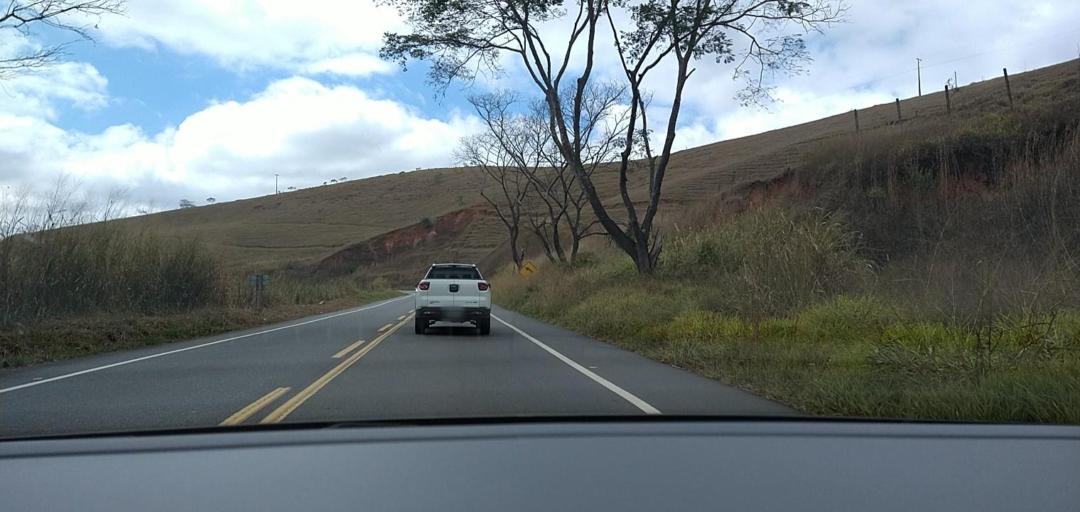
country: BR
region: Minas Gerais
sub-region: Ponte Nova
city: Ponte Nova
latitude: -20.5126
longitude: -42.8911
